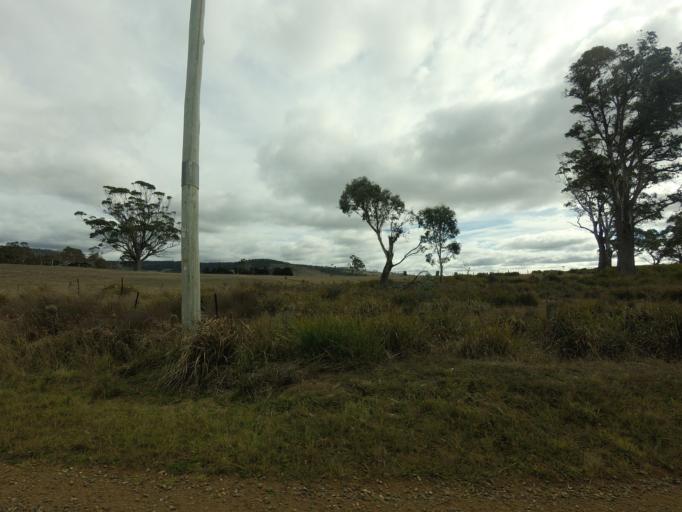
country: AU
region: Tasmania
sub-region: Brighton
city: Bridgewater
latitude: -42.4386
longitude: 147.3857
